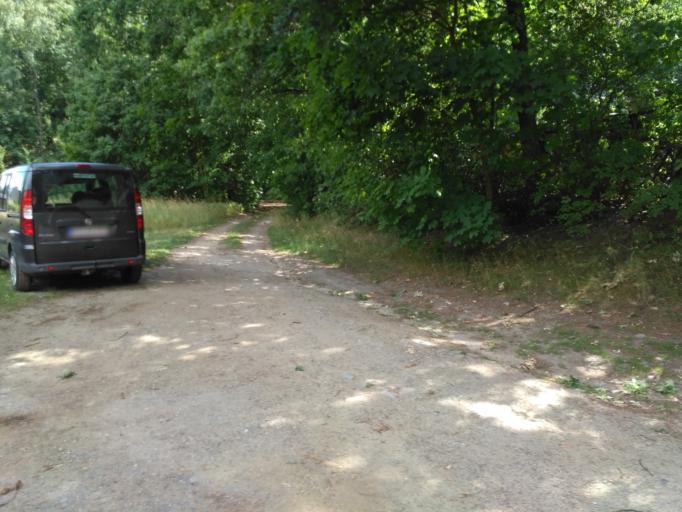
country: DE
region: Saxony
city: Konigsbruck
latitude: 51.2546
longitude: 13.9078
